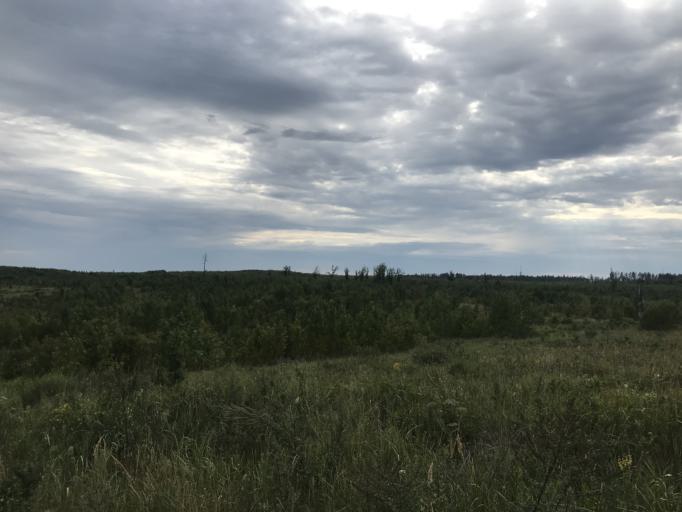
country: RU
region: Samara
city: Tol'yatti
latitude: 53.4979
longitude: 49.3373
